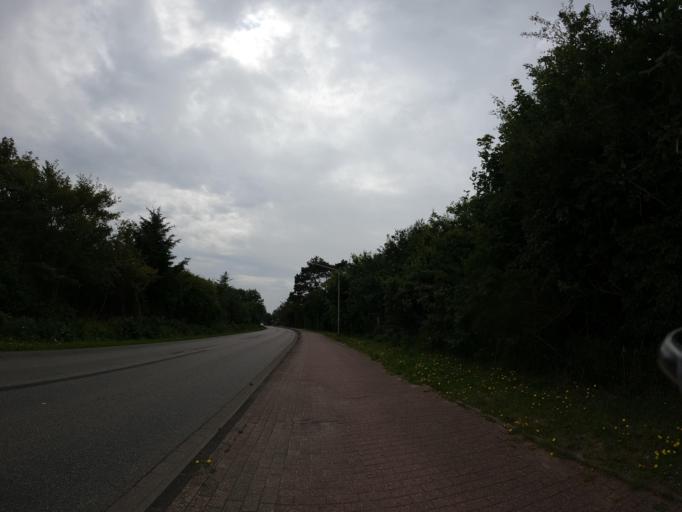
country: DE
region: Schleswig-Holstein
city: Westerland
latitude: 54.9236
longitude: 8.3131
